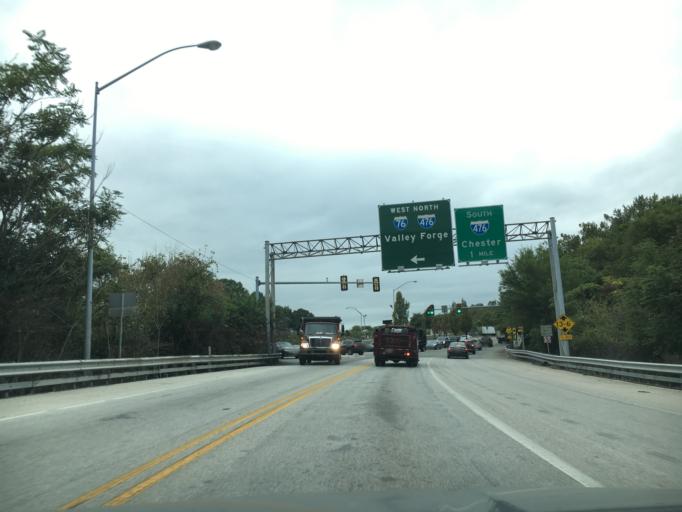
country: US
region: Pennsylvania
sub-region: Montgomery County
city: West Conshohocken
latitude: 40.0671
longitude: -75.3164
